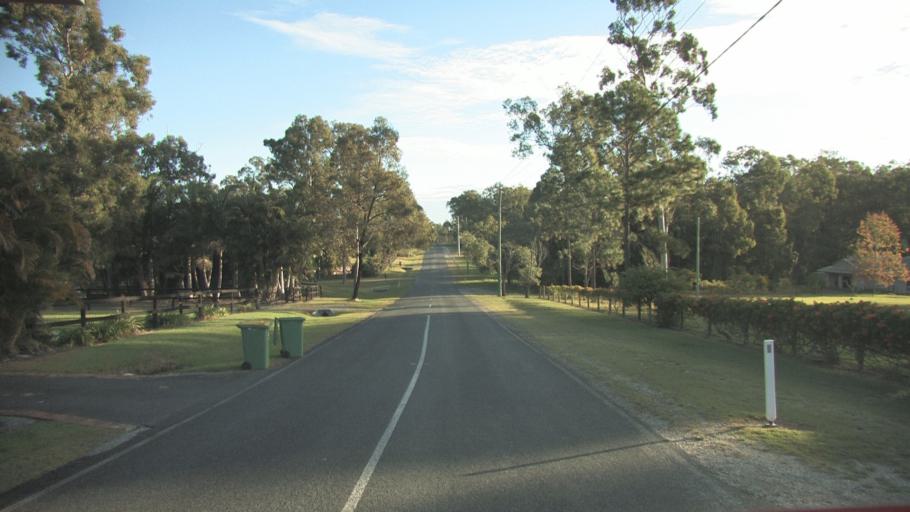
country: AU
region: Queensland
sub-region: Logan
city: Waterford West
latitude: -27.7309
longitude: 153.1436
